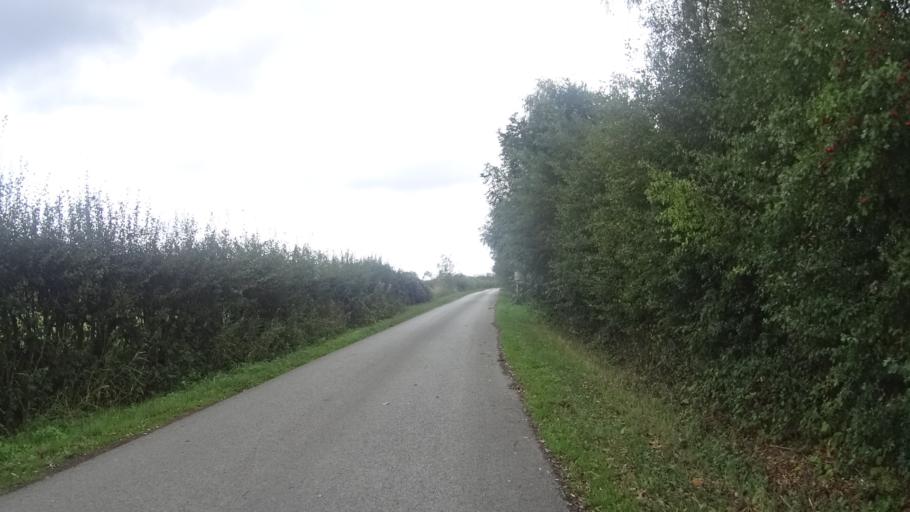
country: FR
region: Nord-Pas-de-Calais
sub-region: Departement du Nord
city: Maroilles
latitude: 50.1424
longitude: 3.7353
